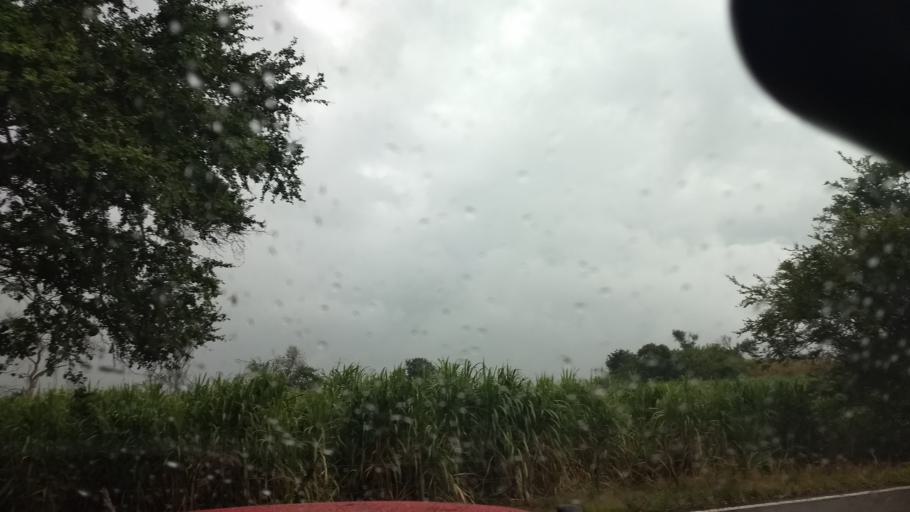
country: MX
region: Jalisco
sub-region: Tonila
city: San Marcos
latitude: 19.4402
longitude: -103.4902
